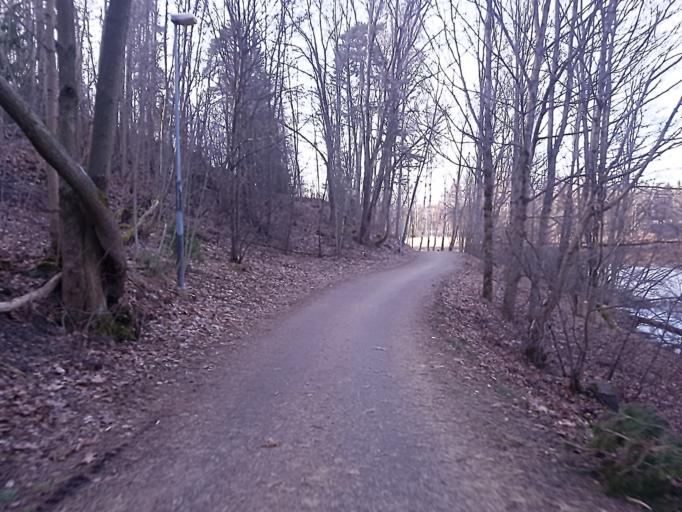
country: FI
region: Uusimaa
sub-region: Helsinki
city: Helsinki
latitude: 60.2415
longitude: 24.9716
